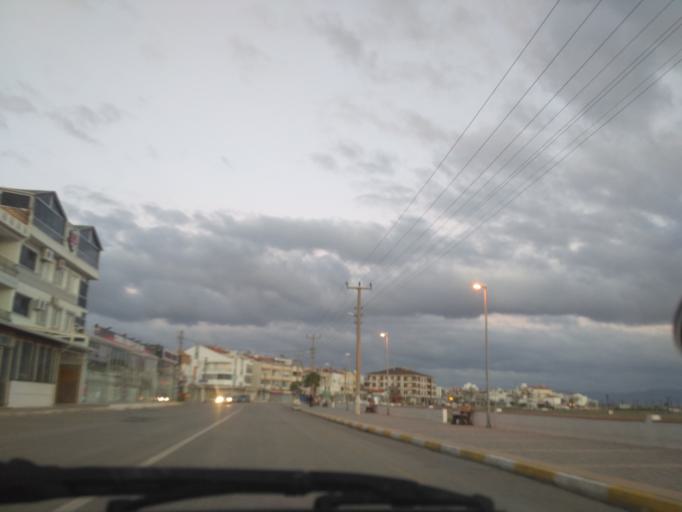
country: TR
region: Balikesir
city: Ayvalik
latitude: 39.2692
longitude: 26.6624
